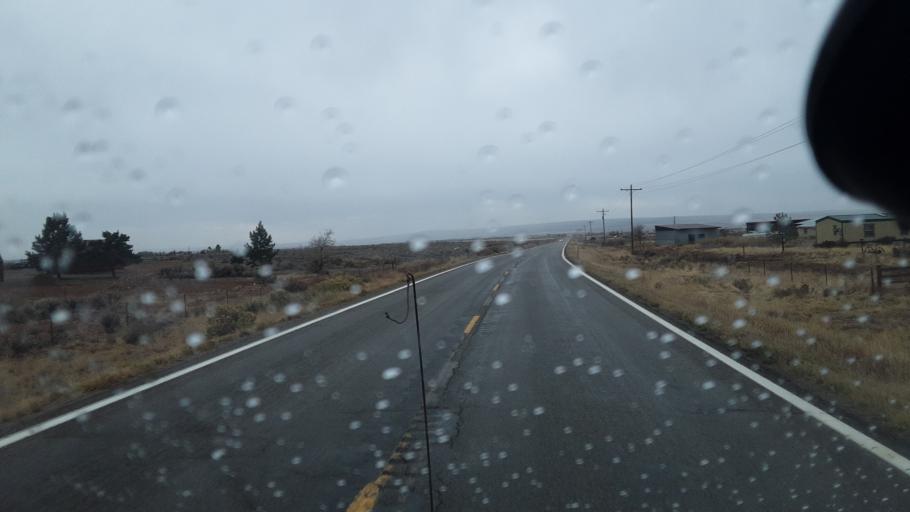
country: US
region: Colorado
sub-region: Montezuma County
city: Mancos
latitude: 37.1321
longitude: -108.1313
